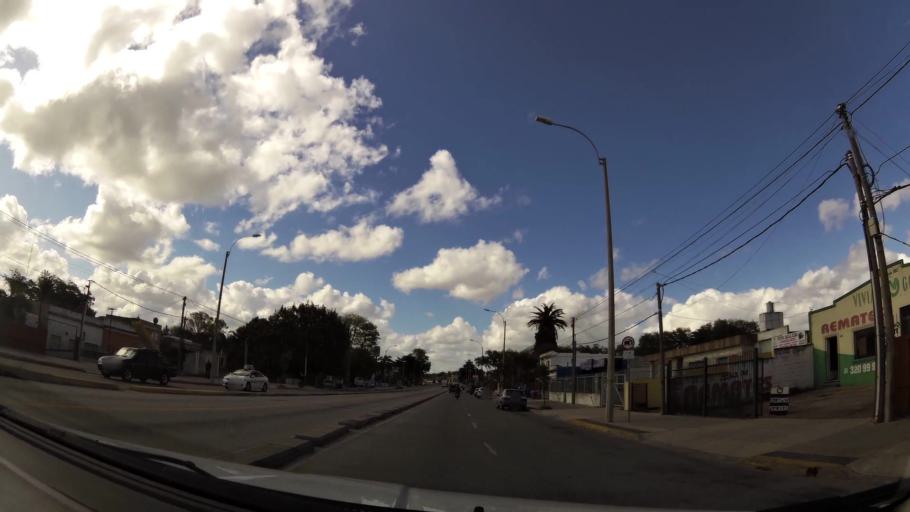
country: UY
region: Canelones
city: La Paz
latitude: -34.8147
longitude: -56.2204
